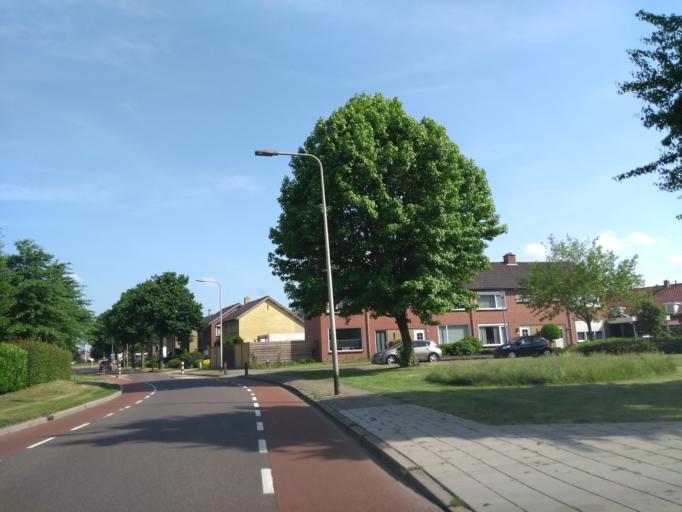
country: DE
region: Lower Saxony
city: Nordhorn
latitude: 52.3782
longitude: 7.0057
